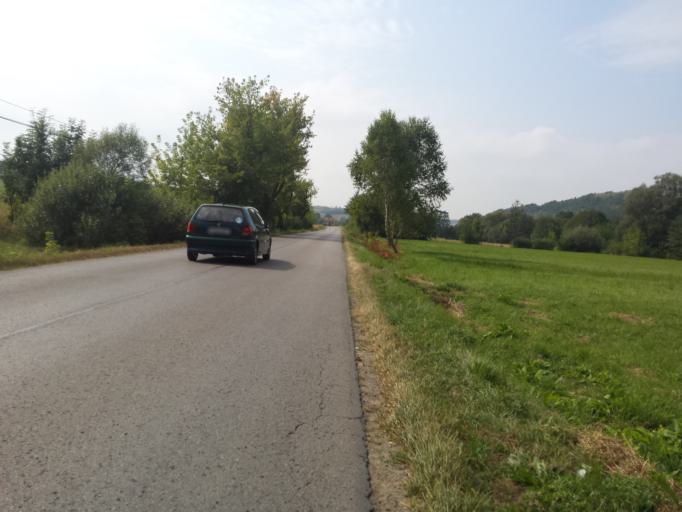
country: PL
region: Subcarpathian Voivodeship
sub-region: Powiat rzeszowski
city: Blazowa
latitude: 49.8748
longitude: 22.1180
